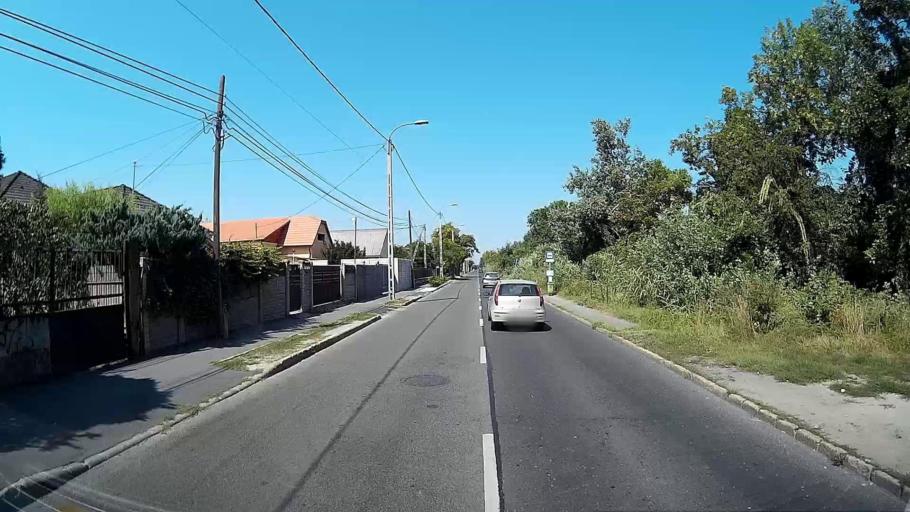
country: HU
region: Budapest
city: Budapest XXIII. keruelet
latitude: 47.4174
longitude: 19.1403
